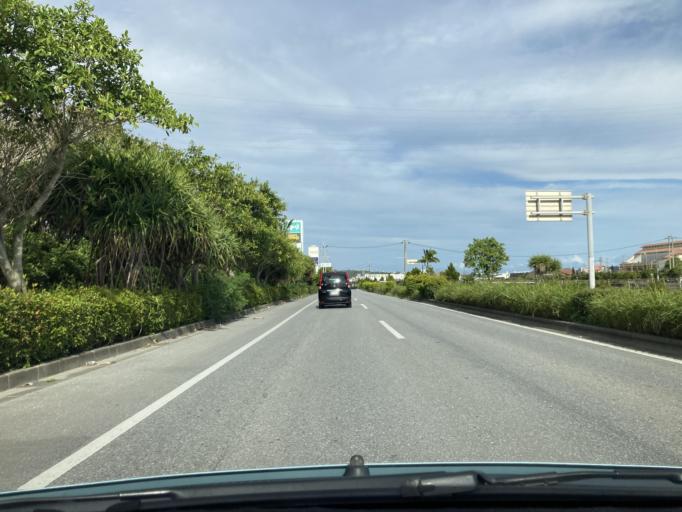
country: JP
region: Okinawa
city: Katsuren-haebaru
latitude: 26.3342
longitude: 127.8413
